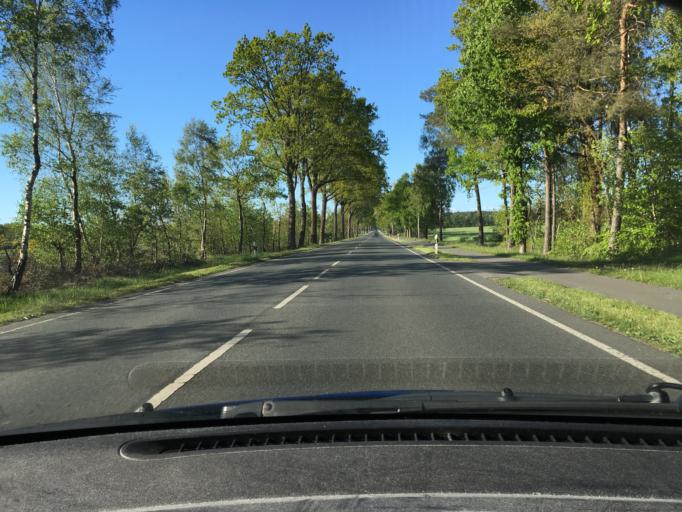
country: DE
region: Lower Saxony
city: Soltau
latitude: 53.0293
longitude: 9.8515
